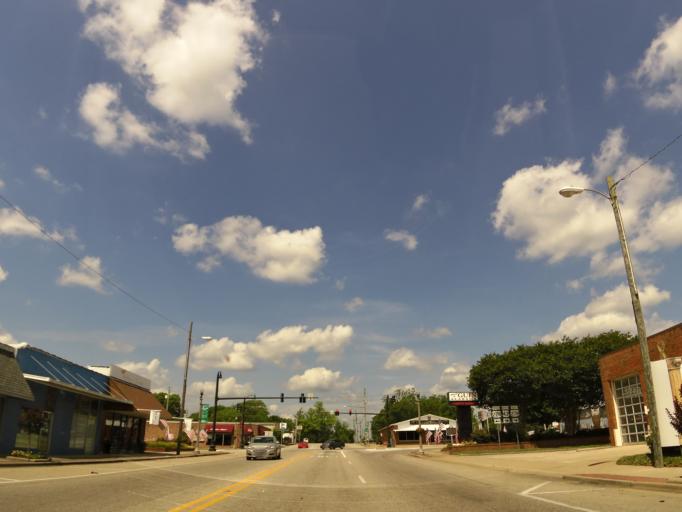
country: US
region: Alabama
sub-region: Marion County
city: Guin
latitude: 33.9657
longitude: -87.9141
